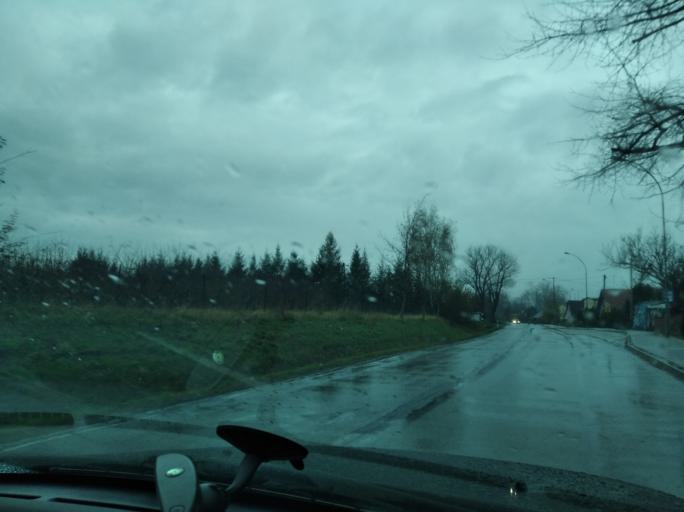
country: PL
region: Subcarpathian Voivodeship
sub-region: Powiat lancucki
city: Albigowa
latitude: 50.0286
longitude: 22.2274
